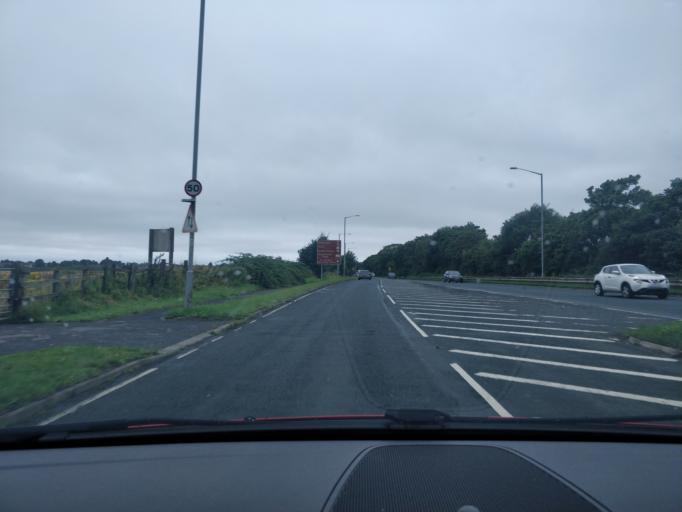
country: GB
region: England
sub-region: Lancashire
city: Banks
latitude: 53.6747
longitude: -2.9308
